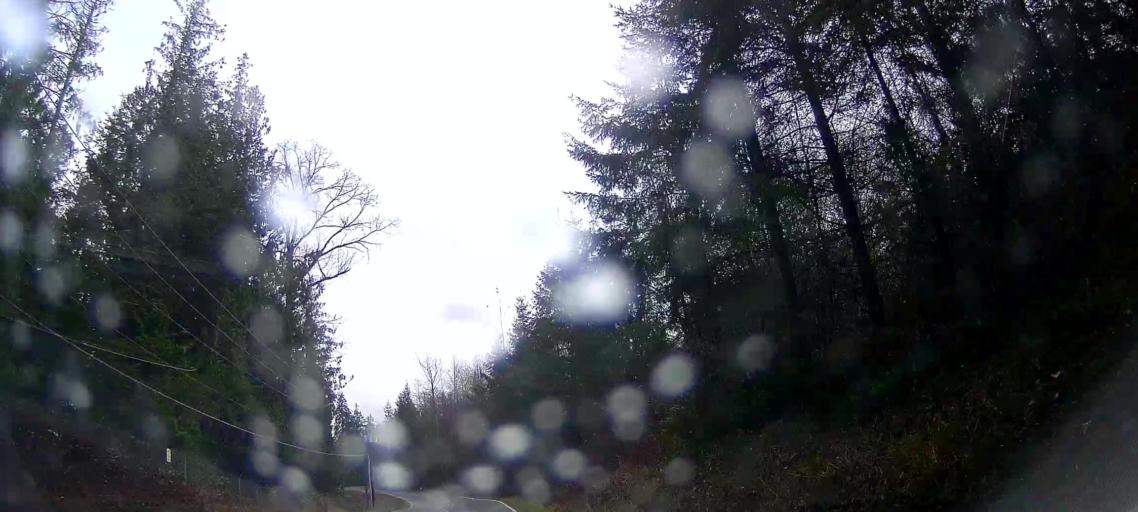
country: US
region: Washington
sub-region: Skagit County
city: Clear Lake
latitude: 48.4708
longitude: -122.1836
